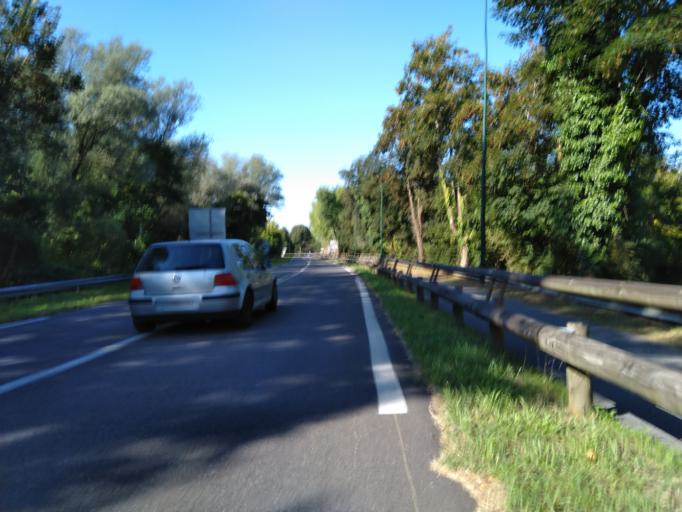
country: FR
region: Aquitaine
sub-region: Departement des Landes
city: Saint-Paul-les-Dax
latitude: 43.7325
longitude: -1.0340
